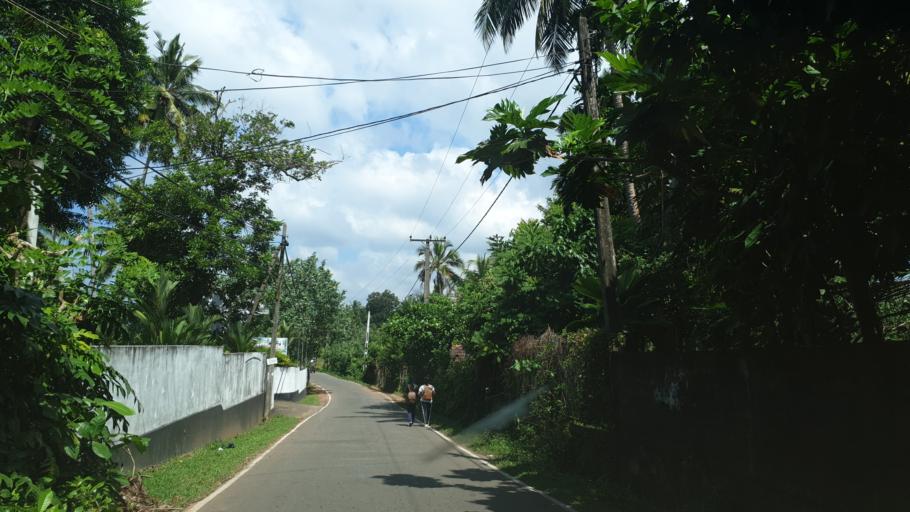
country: LK
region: Western
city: Panadura
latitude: 6.6773
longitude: 79.9397
